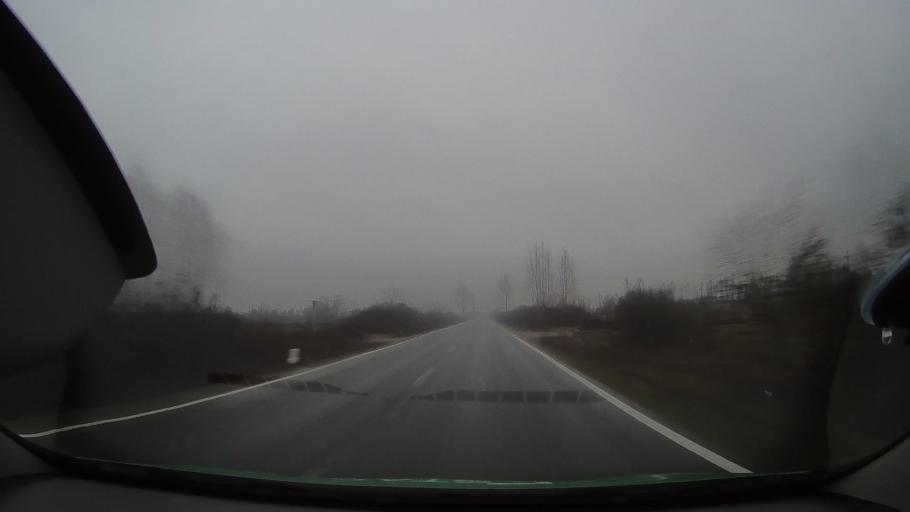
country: RO
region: Bihor
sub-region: Comuna Tinca
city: Tinca
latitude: 46.7514
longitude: 21.9373
